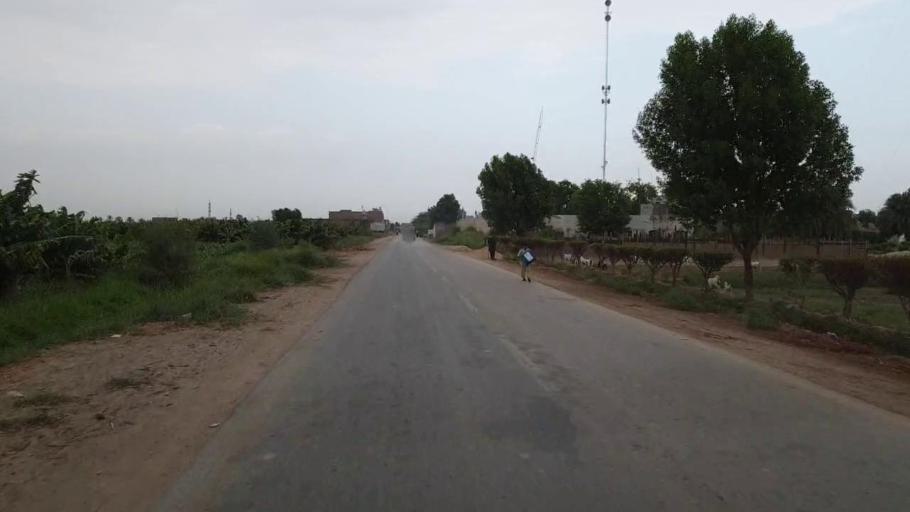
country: PK
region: Sindh
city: Bandhi
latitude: 26.5898
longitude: 68.2957
